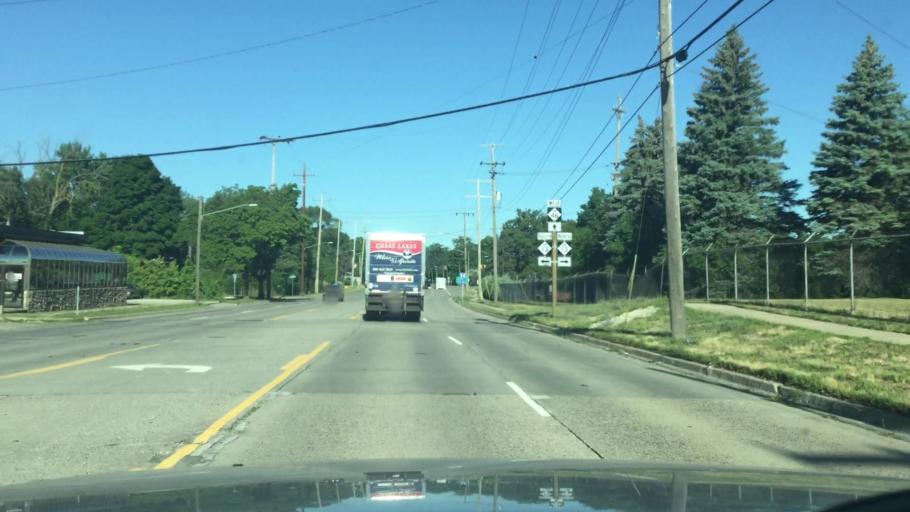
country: US
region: Michigan
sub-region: Saginaw County
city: Saginaw
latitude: 43.4101
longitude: -83.9511
